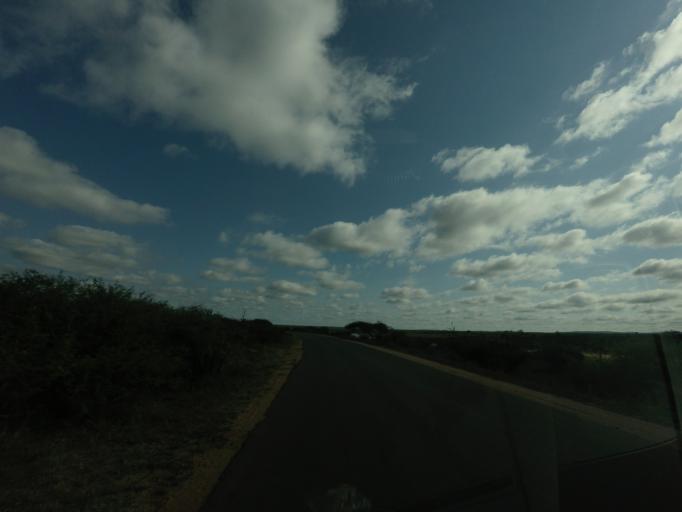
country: ZA
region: Mpumalanga
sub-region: Ehlanzeni District
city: Komatipoort
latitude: -25.1512
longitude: 31.9397
